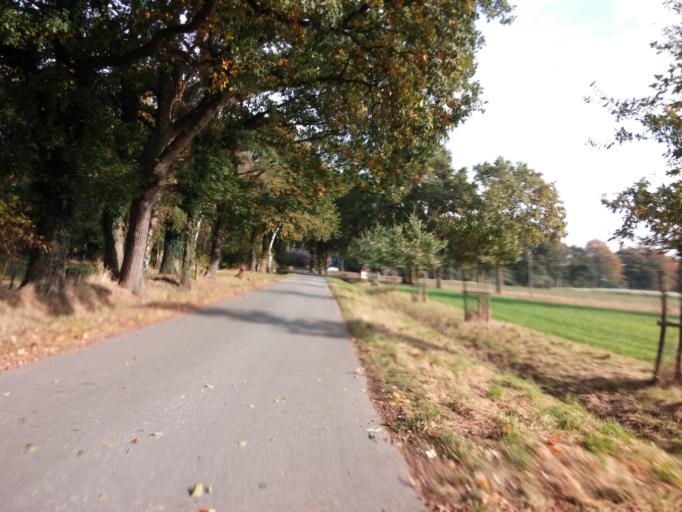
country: DE
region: North Rhine-Westphalia
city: Dorsten
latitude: 51.6231
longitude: 6.9986
